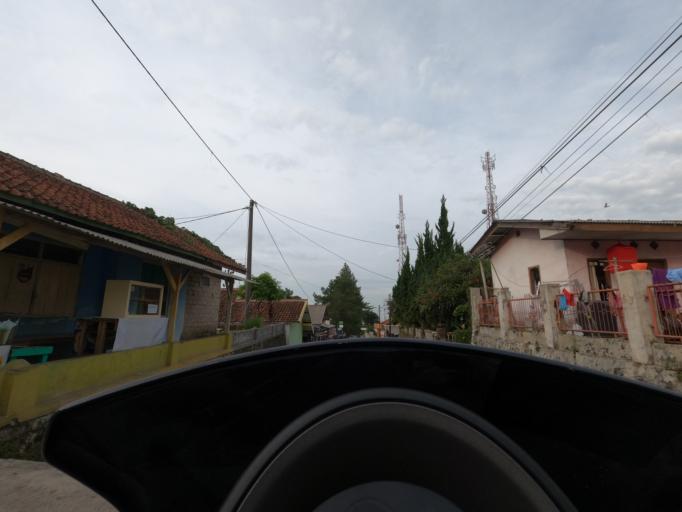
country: ID
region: West Java
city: Lembang
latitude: -6.7323
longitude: 107.6472
